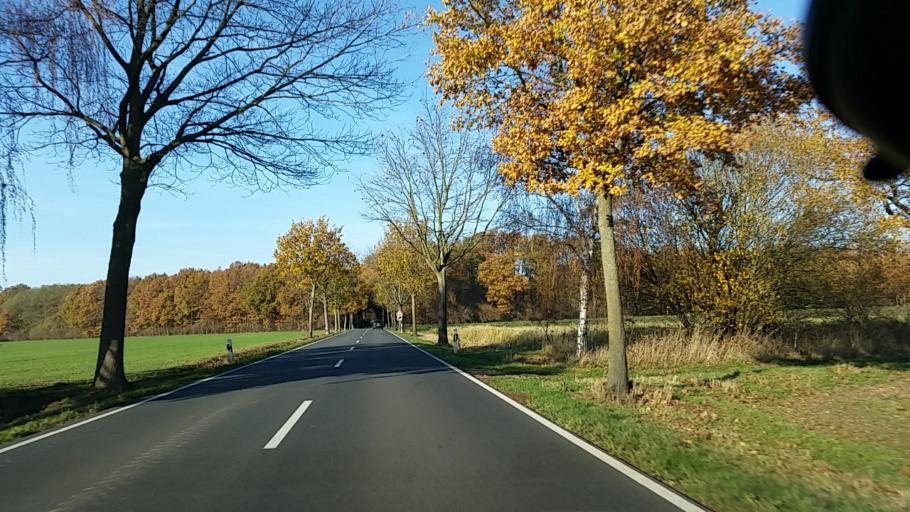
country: DE
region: Saxony-Anhalt
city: Jubar
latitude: 52.6773
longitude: 10.8393
